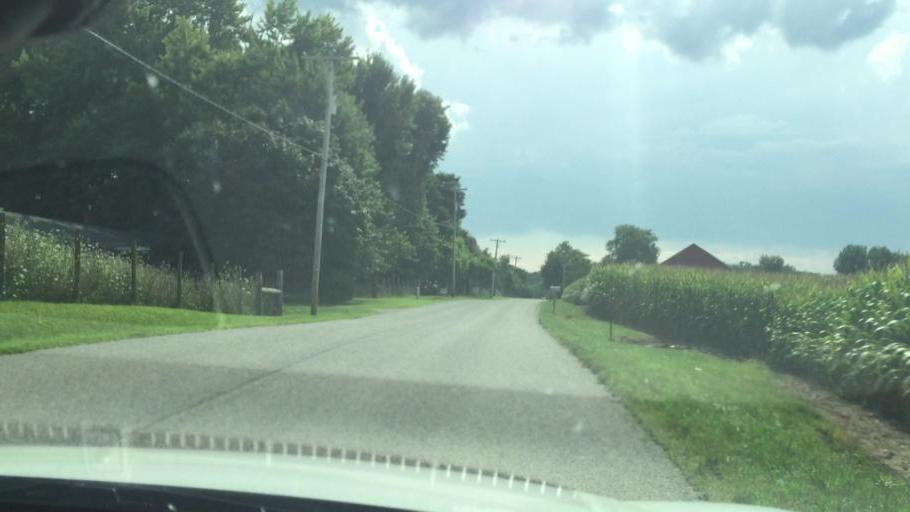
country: US
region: Ohio
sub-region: Clark County
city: Lisbon
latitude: 39.9456
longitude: -83.5836
